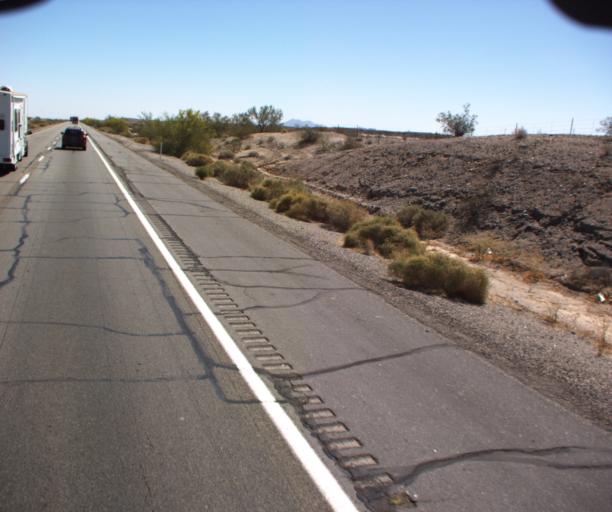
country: US
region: Arizona
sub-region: Yuma County
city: Wellton
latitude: 32.6570
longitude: -114.2435
